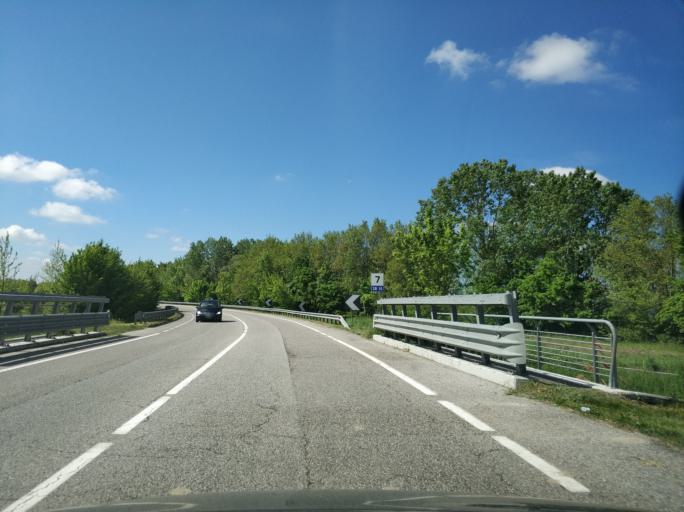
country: IT
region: Veneto
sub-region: Provincia di Venezia
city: Arino
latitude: 45.4449
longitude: 12.0393
